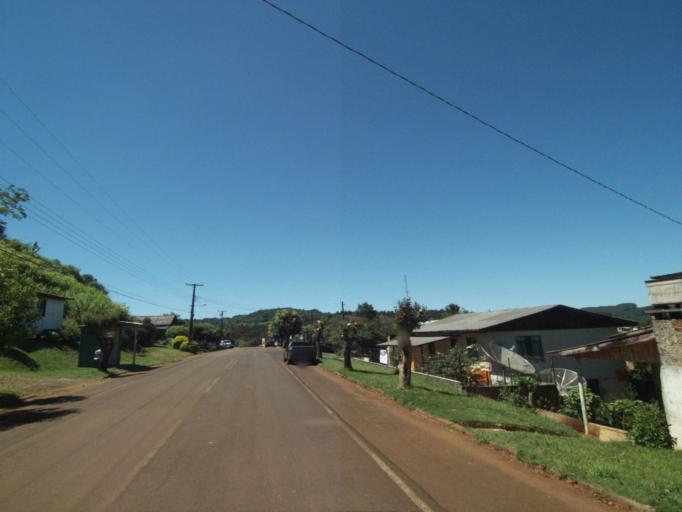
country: BR
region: Parana
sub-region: Pato Branco
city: Pato Branco
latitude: -26.2693
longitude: -52.7754
